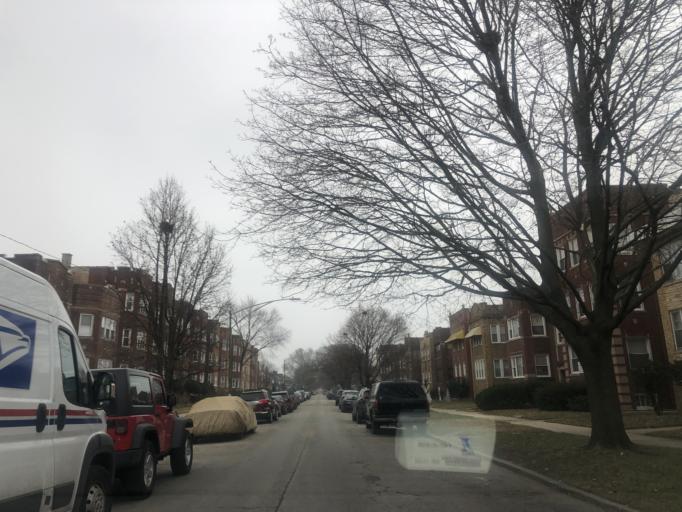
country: US
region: Illinois
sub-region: Cook County
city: Evergreen Park
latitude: 41.7493
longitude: -87.6113
